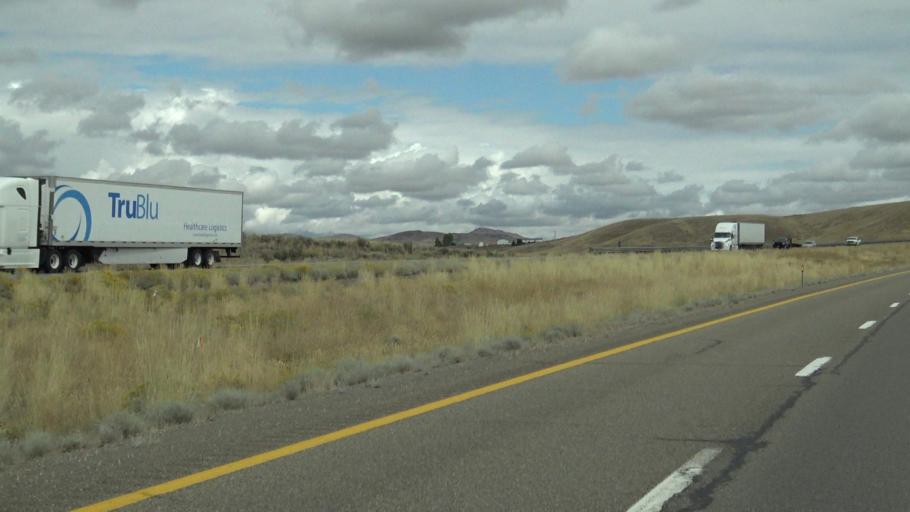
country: US
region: Nevada
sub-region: Elko County
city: Elko
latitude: 40.8910
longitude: -115.7124
